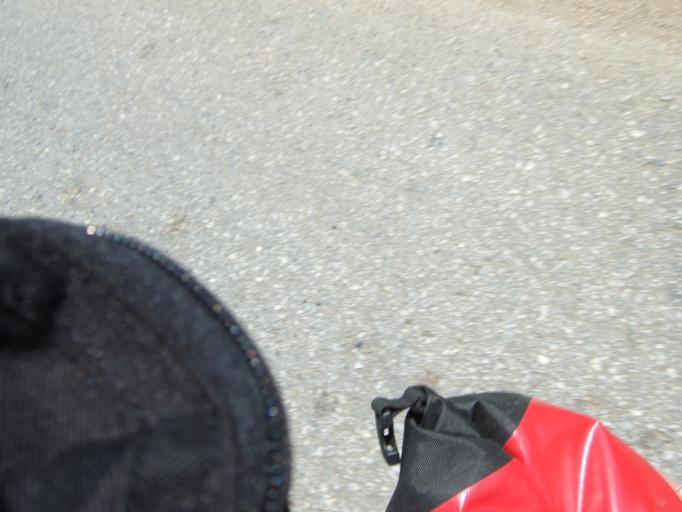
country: GR
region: Central Macedonia
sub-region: Nomos Chalkidikis
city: Nea Roda
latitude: 40.3717
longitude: 23.9222
